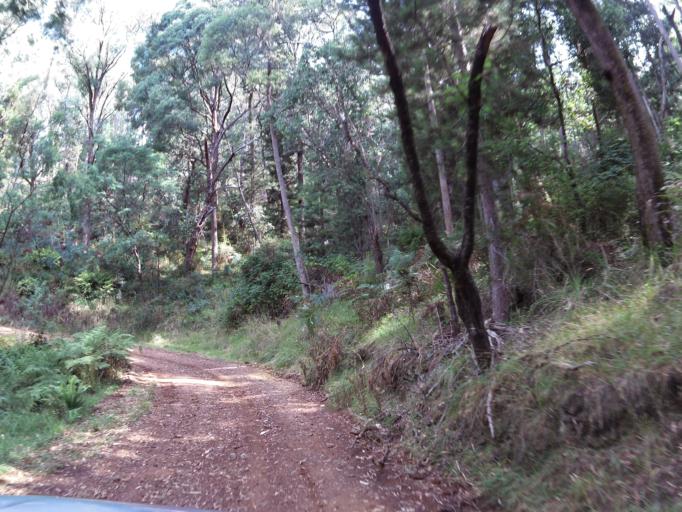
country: AU
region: Victoria
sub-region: Alpine
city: Mount Beauty
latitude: -36.7679
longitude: 147.0145
